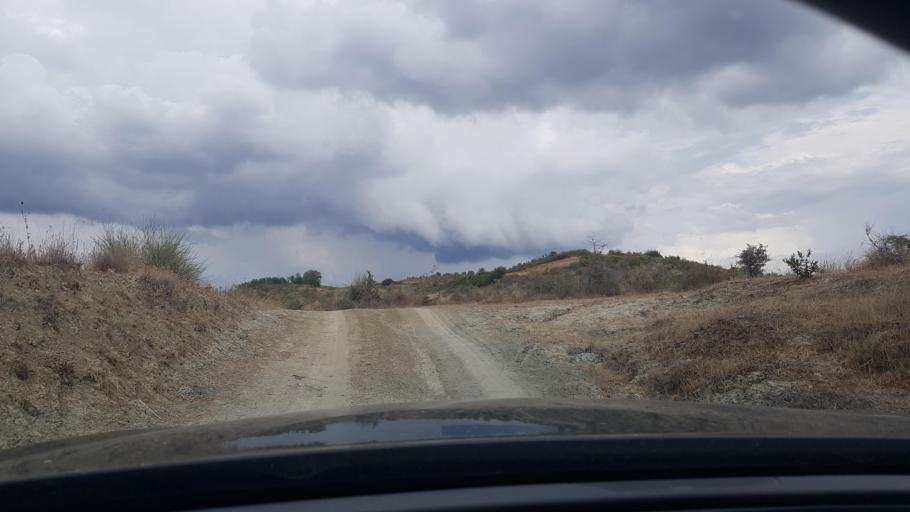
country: AL
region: Durres
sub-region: Rrethi i Durresit
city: Gjepalaj
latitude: 41.2955
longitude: 19.5498
